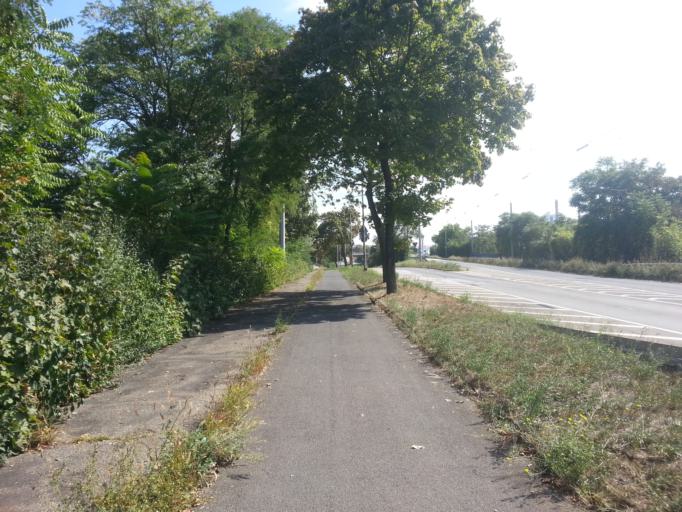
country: DE
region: Baden-Wuerttemberg
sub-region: Karlsruhe Region
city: Mannheim
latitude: 49.5340
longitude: 8.4769
